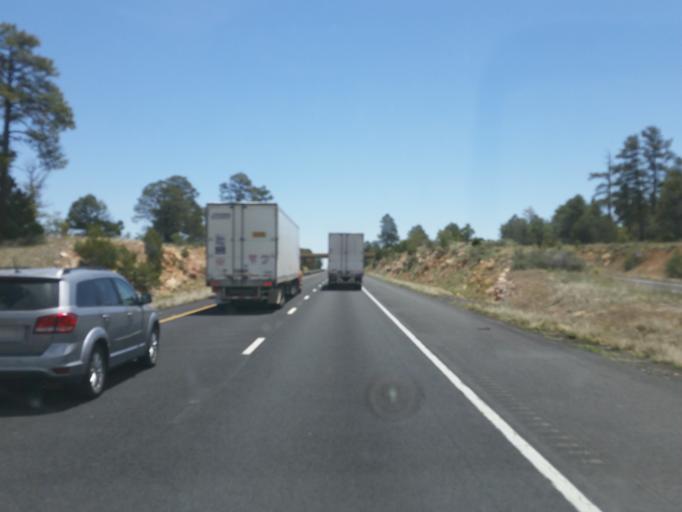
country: US
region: Arizona
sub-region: Coconino County
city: Flagstaff
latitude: 35.2091
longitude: -111.5203
